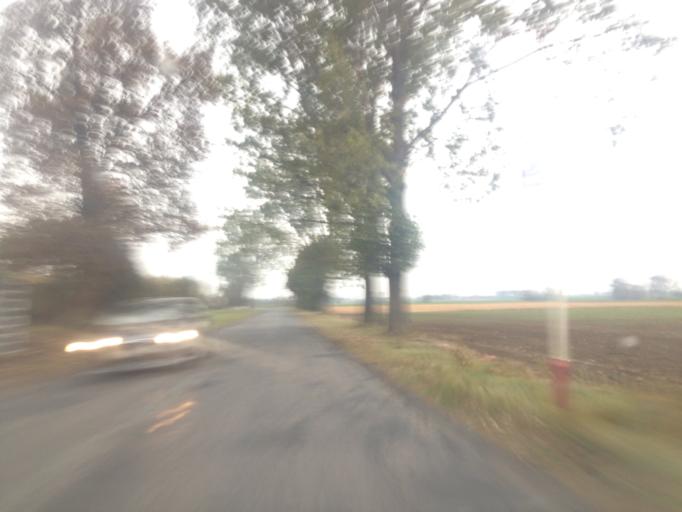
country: PL
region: Greater Poland Voivodeship
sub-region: Powiat poznanski
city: Kleszczewo
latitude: 52.3460
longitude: 17.1551
